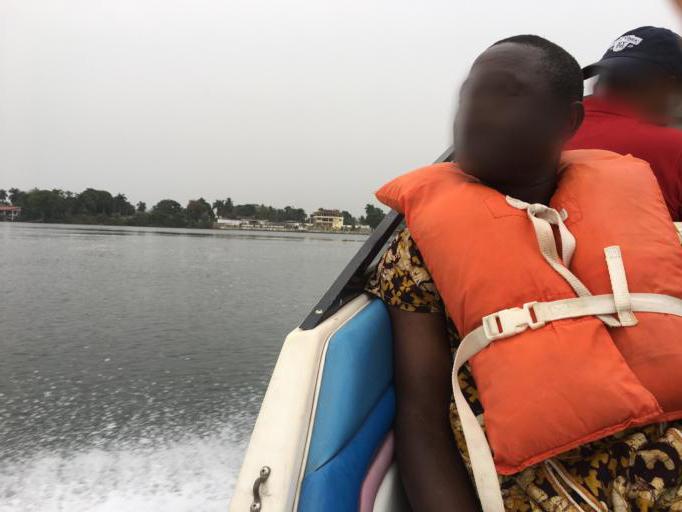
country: LR
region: Montserrado
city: Monrovia
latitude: 6.3915
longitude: -10.7881
